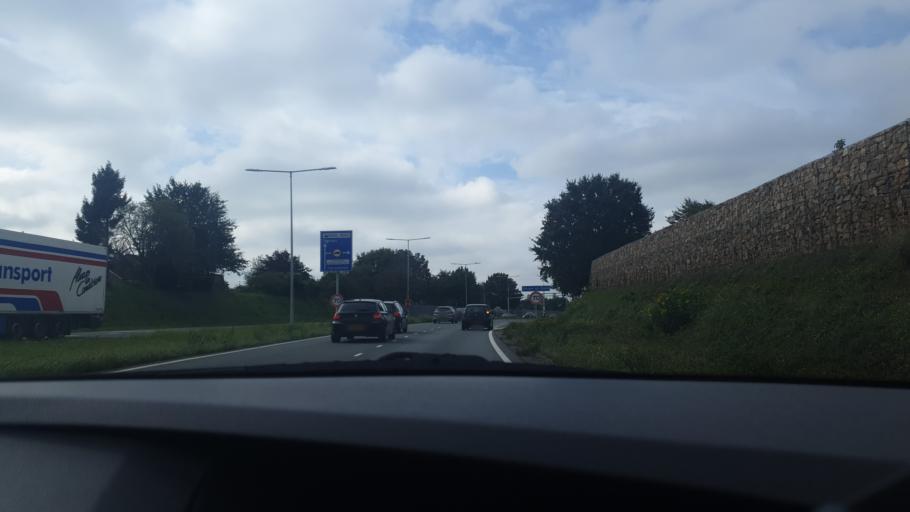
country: NL
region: North Brabant
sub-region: Gemeente Bergen op Zoom
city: Bergen op Zoom
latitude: 51.5121
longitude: 4.2812
